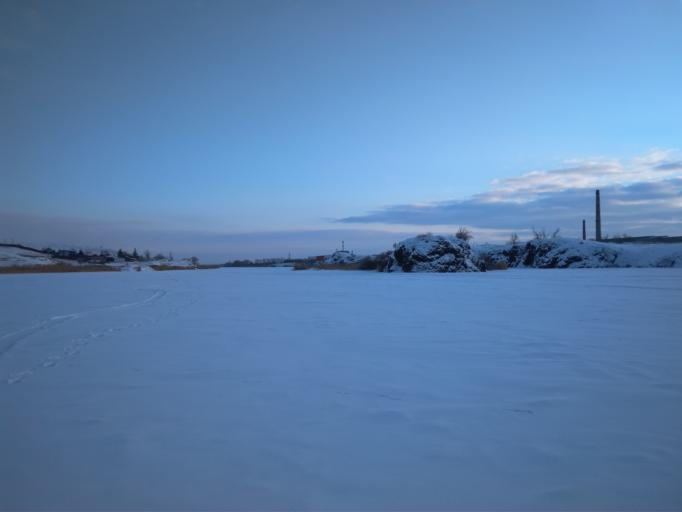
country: RU
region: Chelyabinsk
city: Troitsk
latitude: 54.0771
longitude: 61.5753
